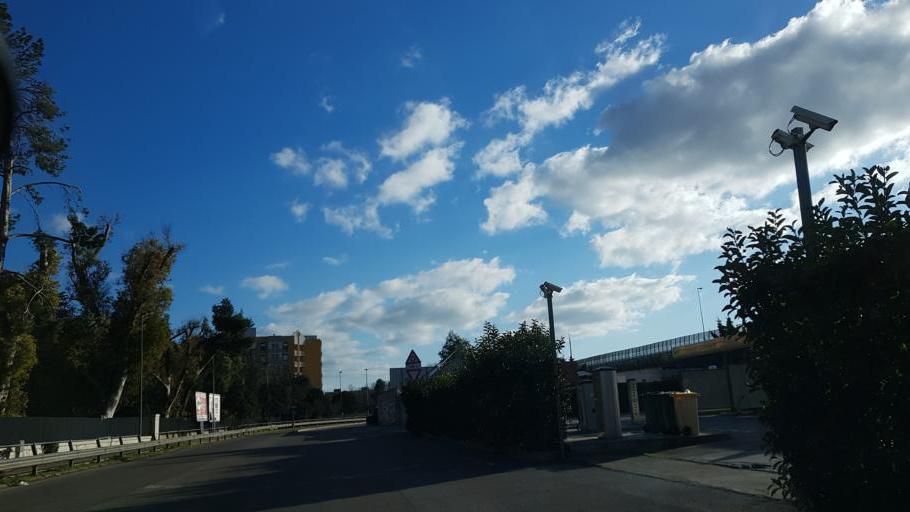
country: IT
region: Apulia
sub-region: Provincia di Brindisi
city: Brindisi
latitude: 40.6280
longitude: 17.9197
